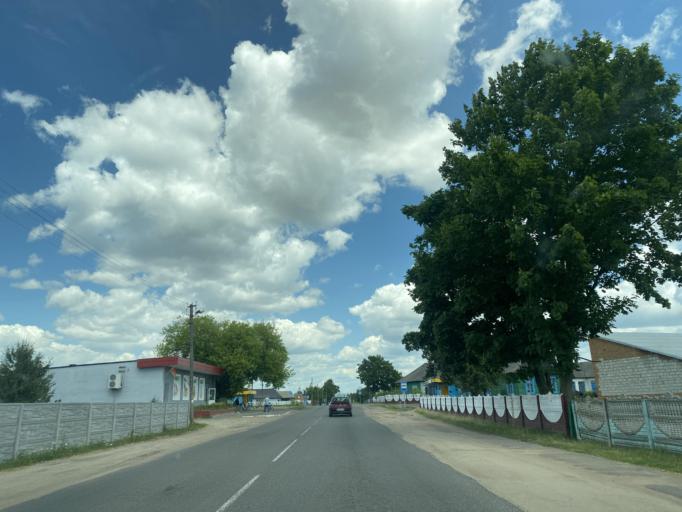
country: BY
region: Brest
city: Ivanava
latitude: 52.1674
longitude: 25.5503
